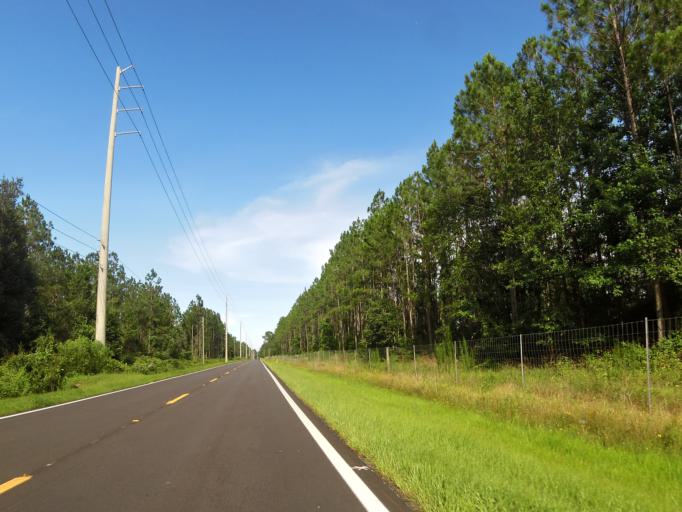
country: US
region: Florida
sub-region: Clay County
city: Green Cove Springs
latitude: 30.0147
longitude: -81.5781
